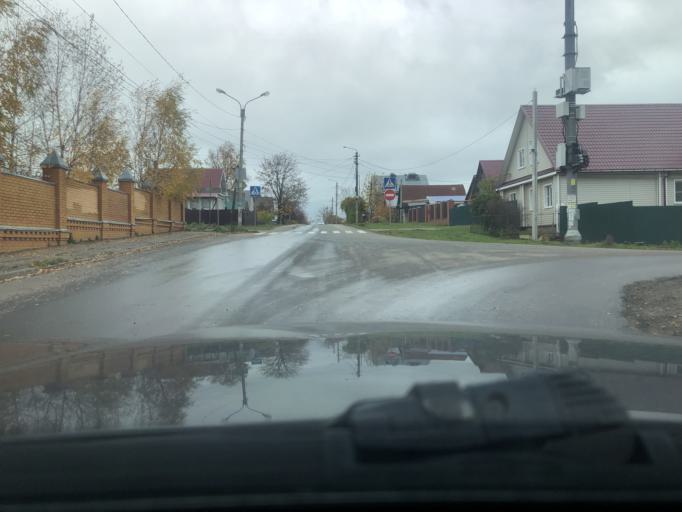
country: RU
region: Moskovskaya
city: Sergiyev Posad
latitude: 56.3076
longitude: 38.1008
